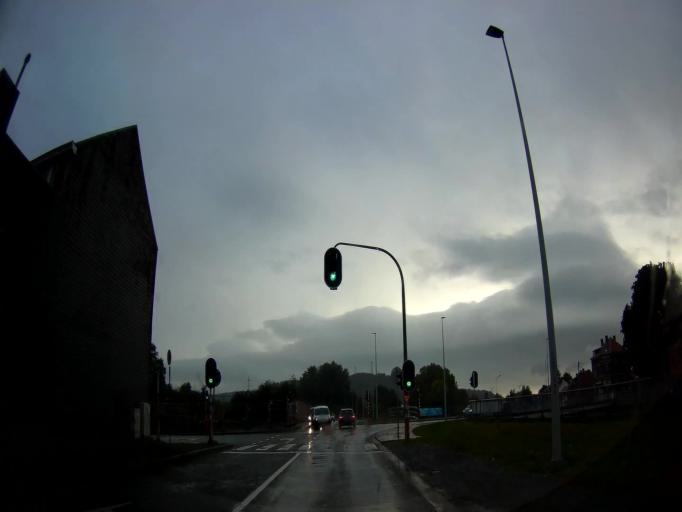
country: BE
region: Wallonia
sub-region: Province de Liege
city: Chaudfontaine
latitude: 50.6099
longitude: 5.6202
